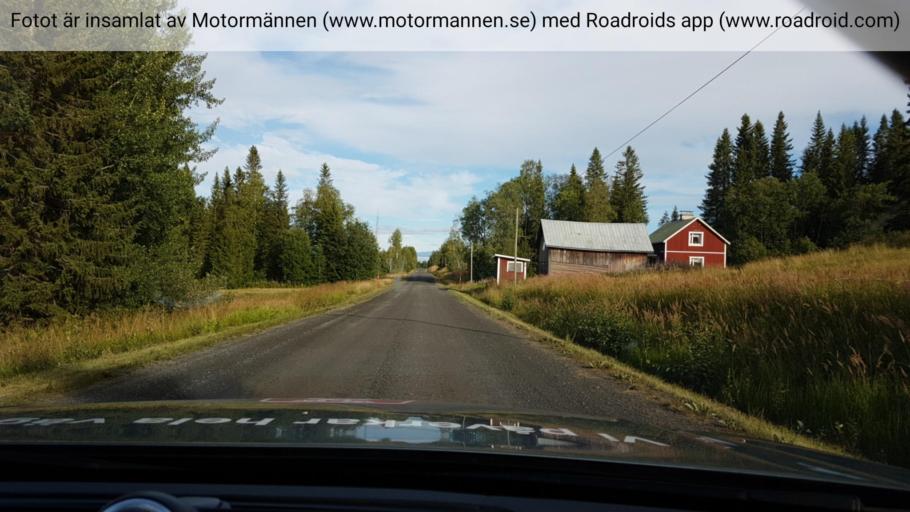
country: SE
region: Jaemtland
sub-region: Stroemsunds Kommun
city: Stroemsund
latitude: 64.1367
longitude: 15.7584
